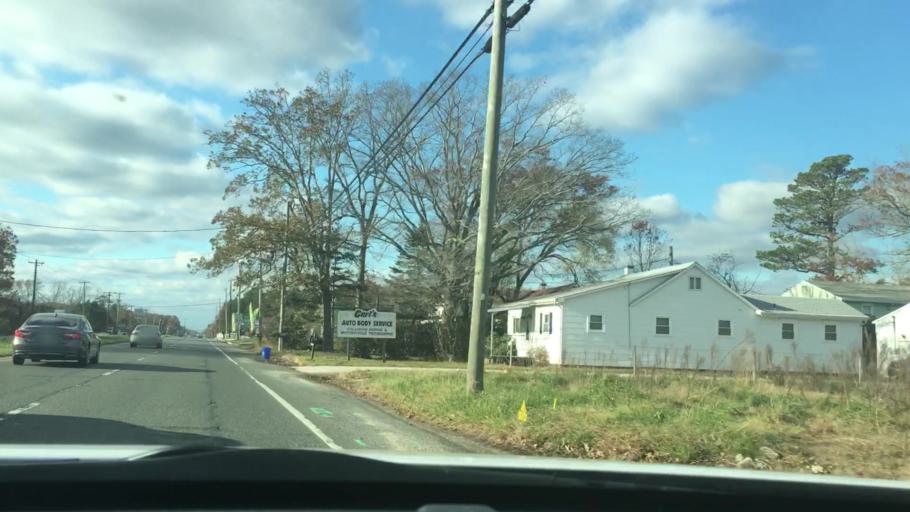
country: US
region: New Jersey
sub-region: Atlantic County
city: Northfield
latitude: 39.4193
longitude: -74.5838
